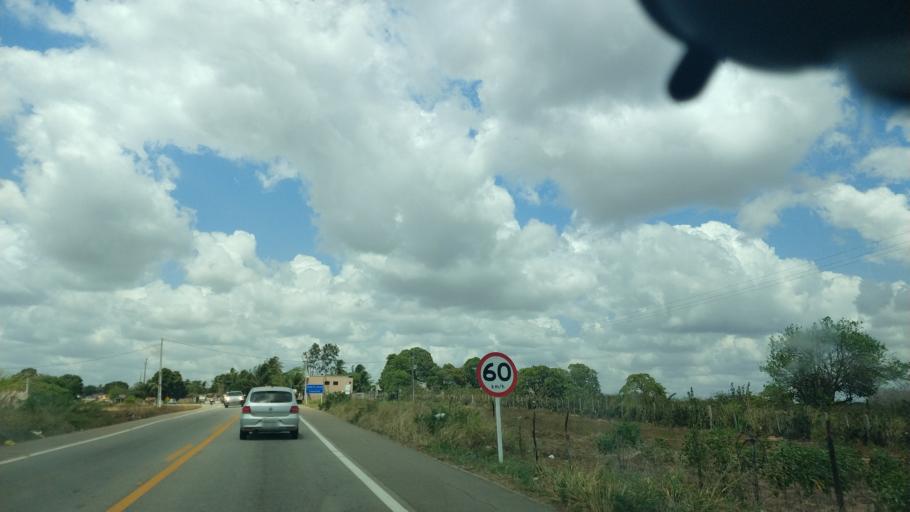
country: BR
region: Rio Grande do Norte
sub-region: Macaiba
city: Macaiba
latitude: -5.9221
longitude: -35.5358
